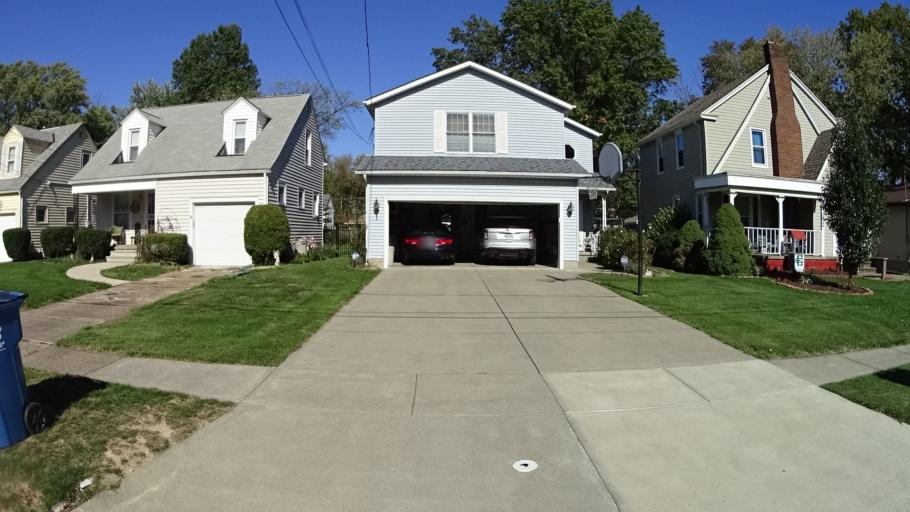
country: US
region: Ohio
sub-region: Lorain County
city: Lorain
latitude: 41.4438
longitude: -82.1811
